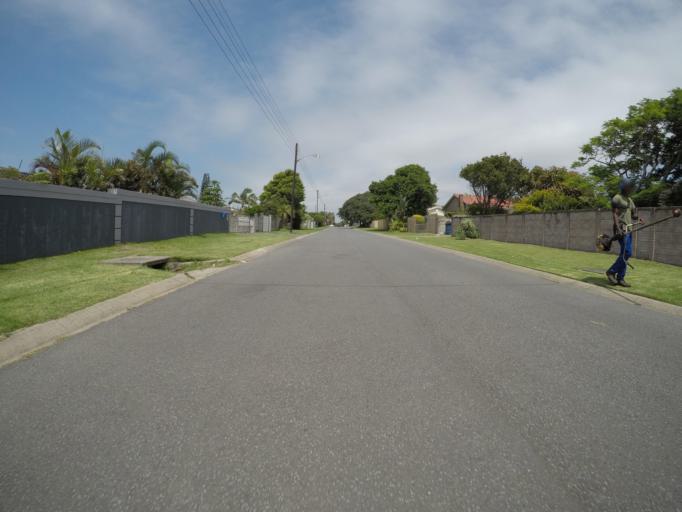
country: ZA
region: Eastern Cape
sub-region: Buffalo City Metropolitan Municipality
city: East London
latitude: -32.9480
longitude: 28.0149
